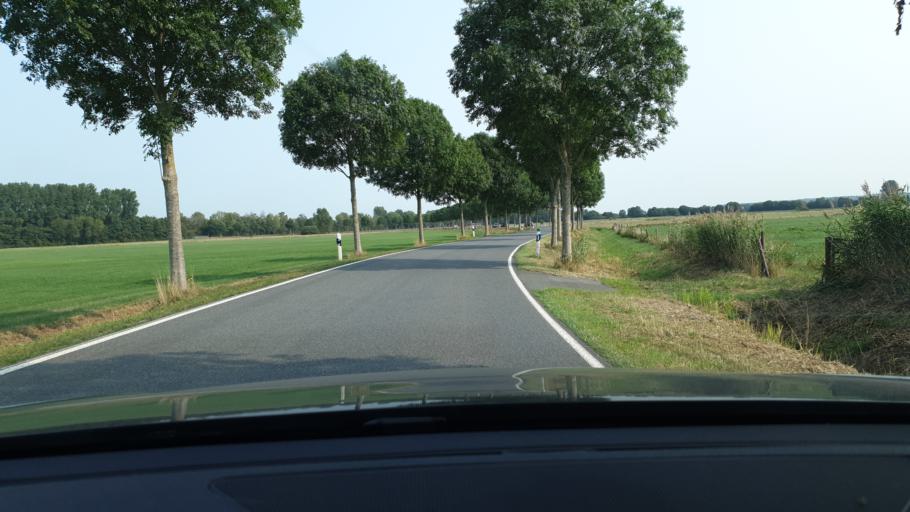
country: DE
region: North Rhine-Westphalia
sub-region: Regierungsbezirk Dusseldorf
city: Kranenburg
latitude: 51.7967
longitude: 6.0090
